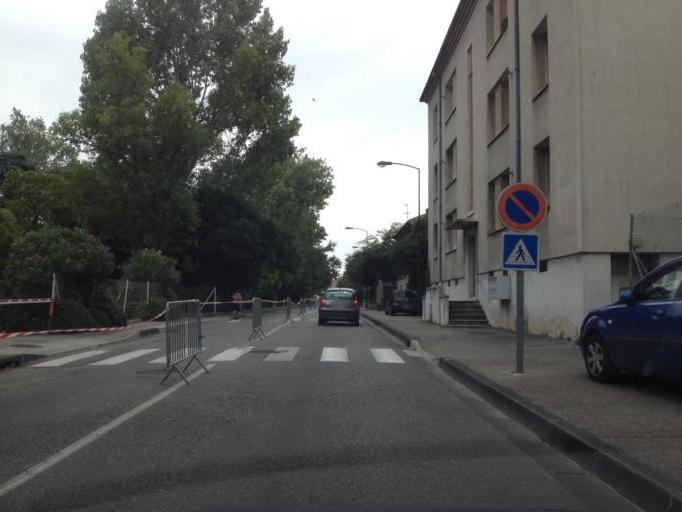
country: FR
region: Rhone-Alpes
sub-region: Departement de la Drome
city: Montelimar
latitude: 44.5610
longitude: 4.7462
